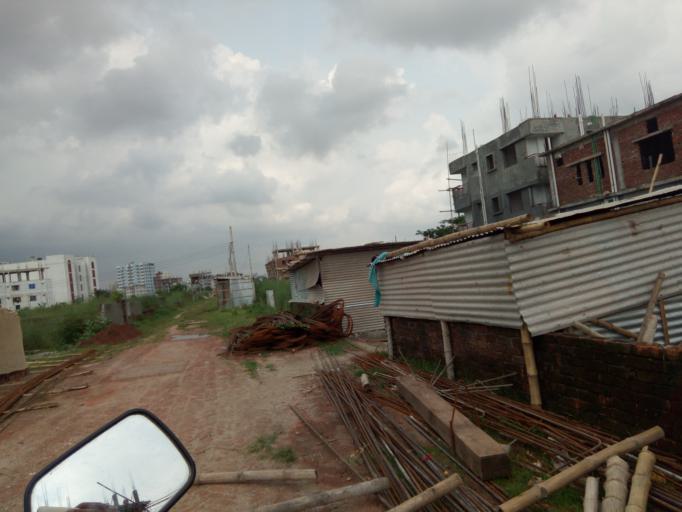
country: BD
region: Dhaka
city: Azimpur
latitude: 23.7501
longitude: 90.3481
